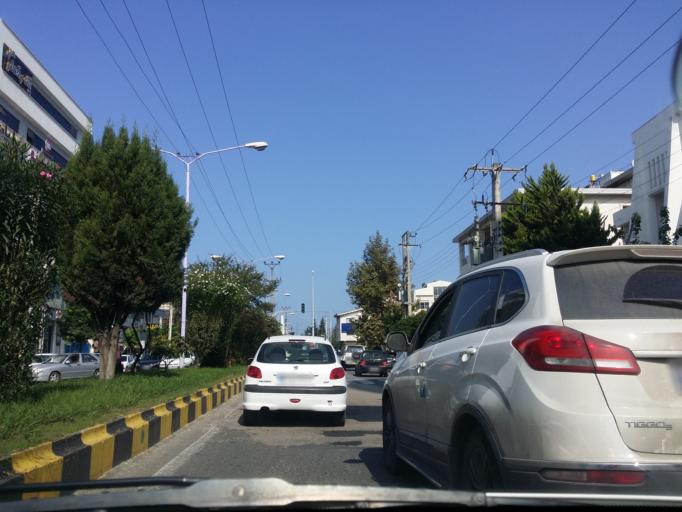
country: IR
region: Mazandaran
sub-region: Nowshahr
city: Nowshahr
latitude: 36.6518
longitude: 51.4948
